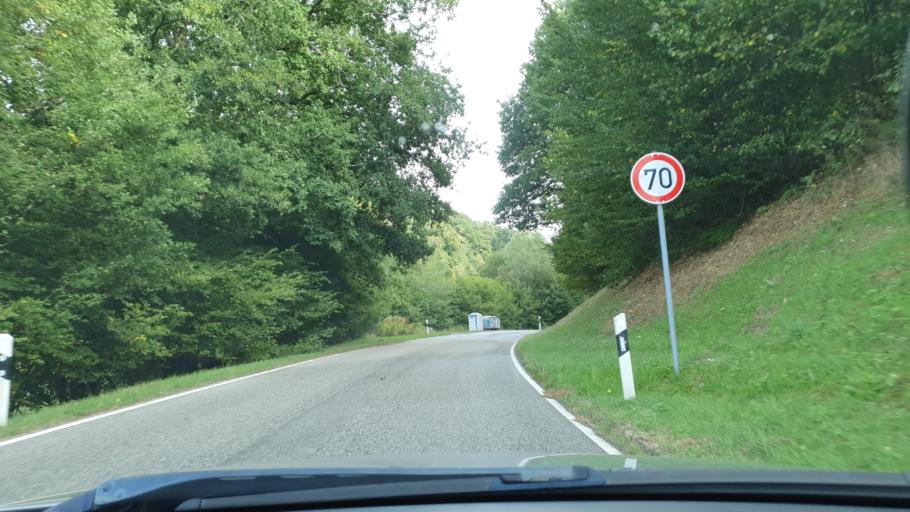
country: DE
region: Rheinland-Pfalz
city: Gerhardsbrunn
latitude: 49.3461
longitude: 7.5102
